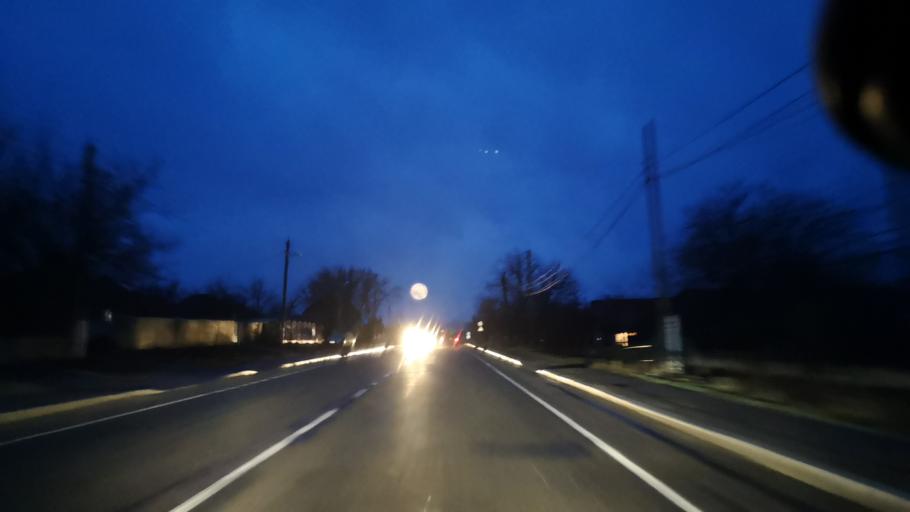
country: MD
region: Orhei
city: Orhei
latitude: 47.4432
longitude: 28.7945
